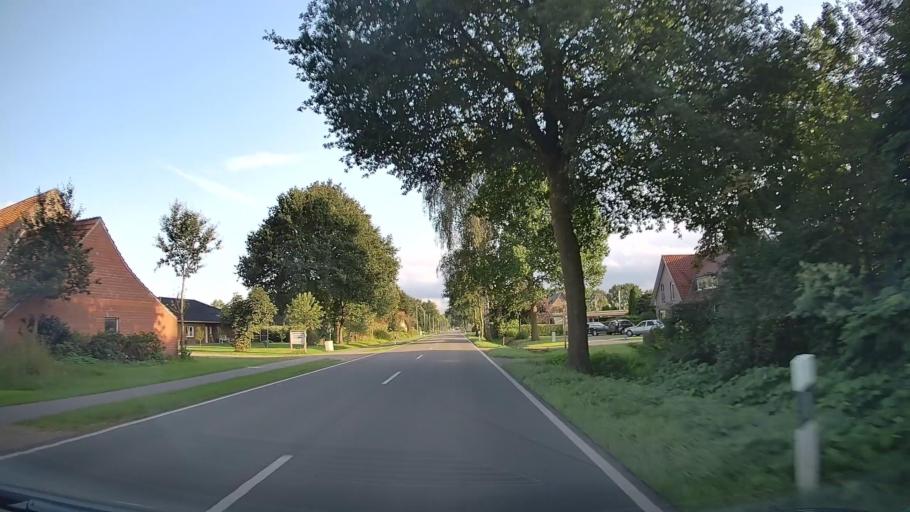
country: DE
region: Lower Saxony
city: Hilkenbrook
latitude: 53.0540
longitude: 7.7290
